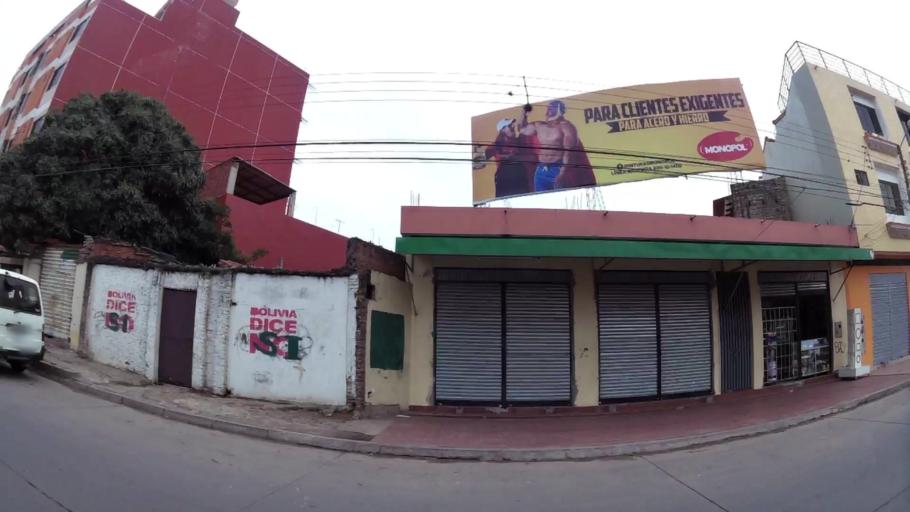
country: BO
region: Santa Cruz
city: Santa Cruz de la Sierra
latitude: -17.7855
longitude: -63.1605
